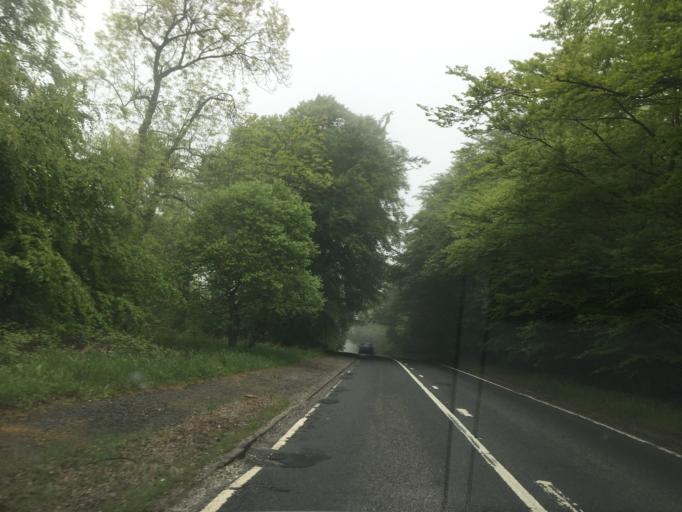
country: GB
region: Scotland
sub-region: Midlothian
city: Penicuik
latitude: 55.8177
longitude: -3.2021
